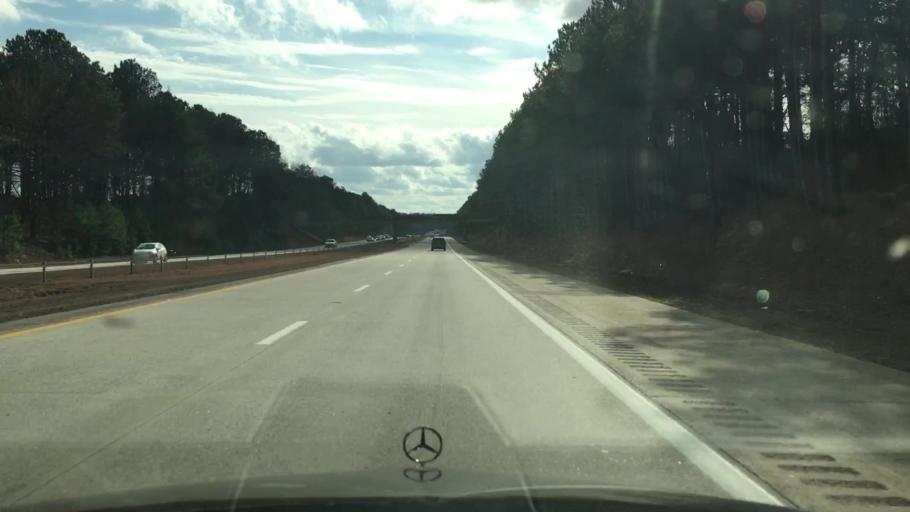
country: US
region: North Carolina
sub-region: Wake County
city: Garner
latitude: 35.5760
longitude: -78.5766
